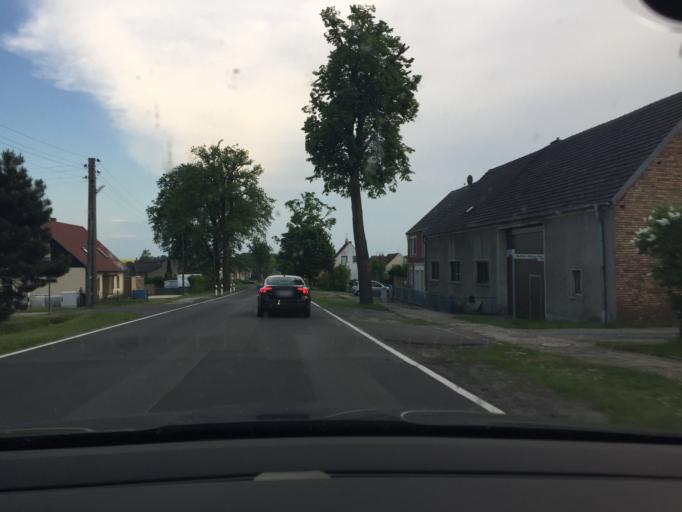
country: DE
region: Brandenburg
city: Treuenbrietzen
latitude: 52.0381
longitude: 12.8075
